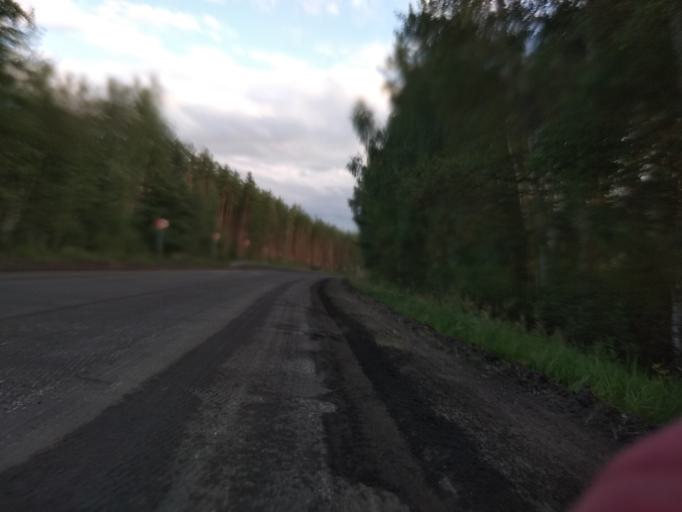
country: RU
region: Moskovskaya
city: Misheronskiy
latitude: 55.6465
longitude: 39.7574
